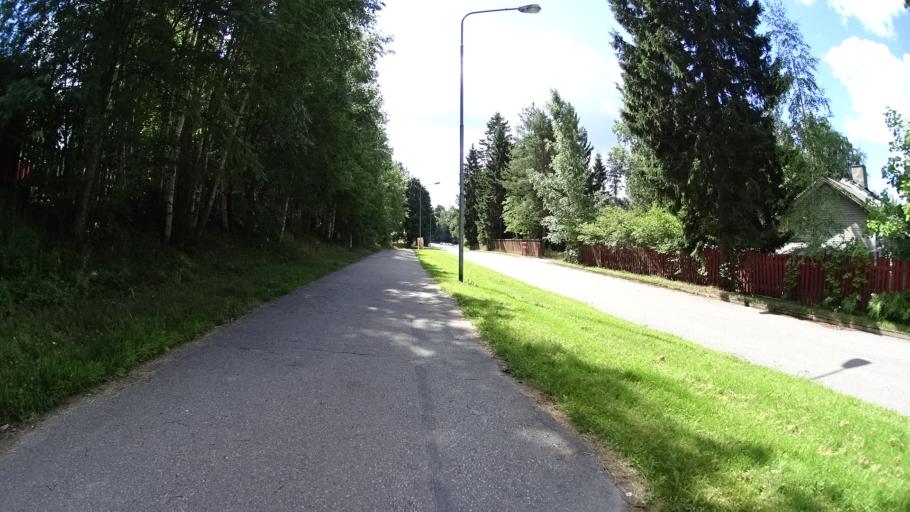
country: FI
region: Uusimaa
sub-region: Helsinki
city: Tuusula
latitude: 60.3943
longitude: 25.0242
